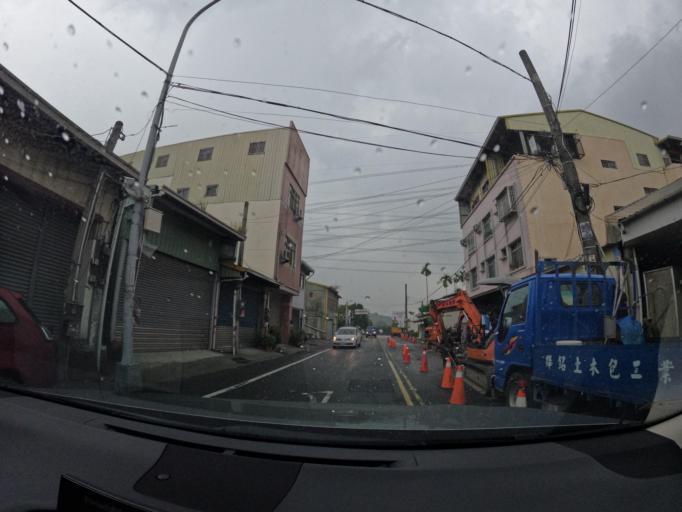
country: TW
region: Taiwan
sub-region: Nantou
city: Nantou
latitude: 23.8805
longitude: 120.7613
